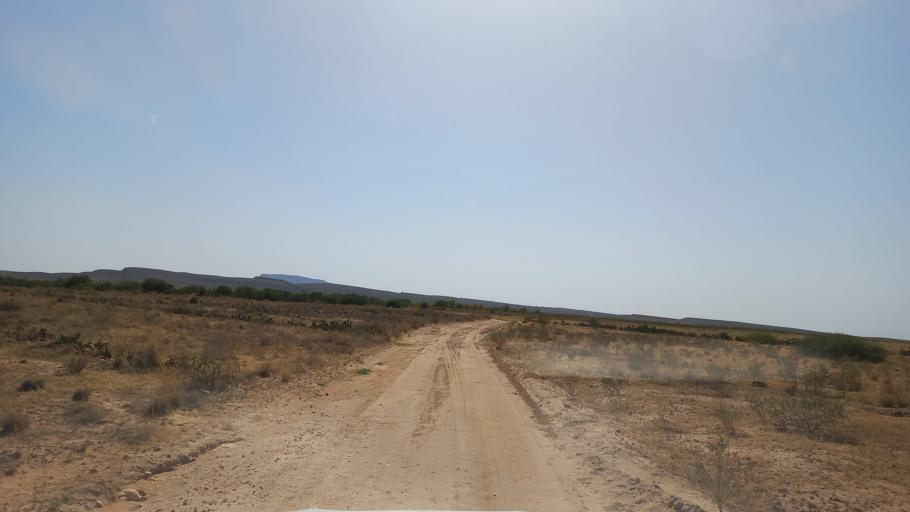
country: TN
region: Al Qasrayn
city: Kasserine
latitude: 35.2148
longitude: 9.0310
